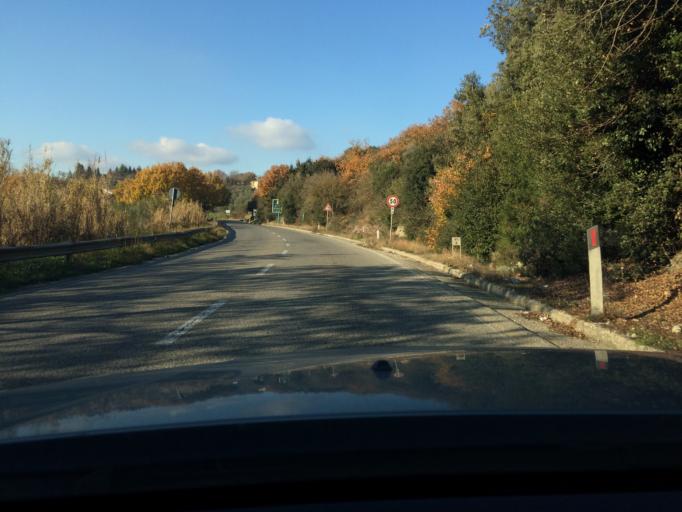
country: IT
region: Umbria
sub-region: Provincia di Terni
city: Fornole
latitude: 42.5563
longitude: 12.4409
